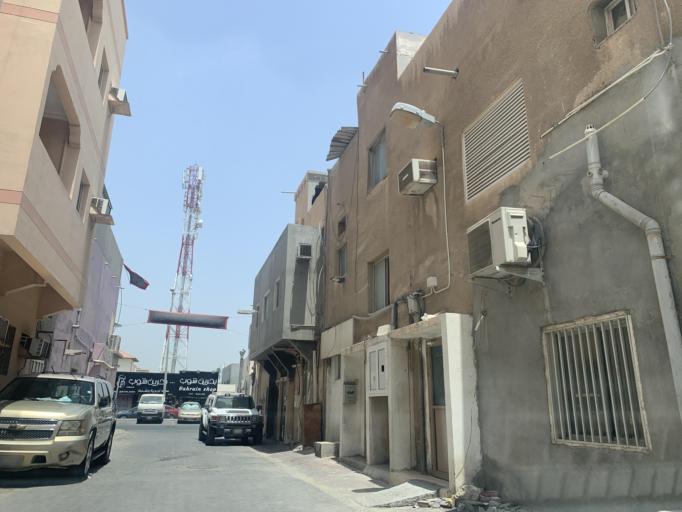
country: BH
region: Central Governorate
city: Madinat Hamad
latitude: 26.1455
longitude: 50.4990
